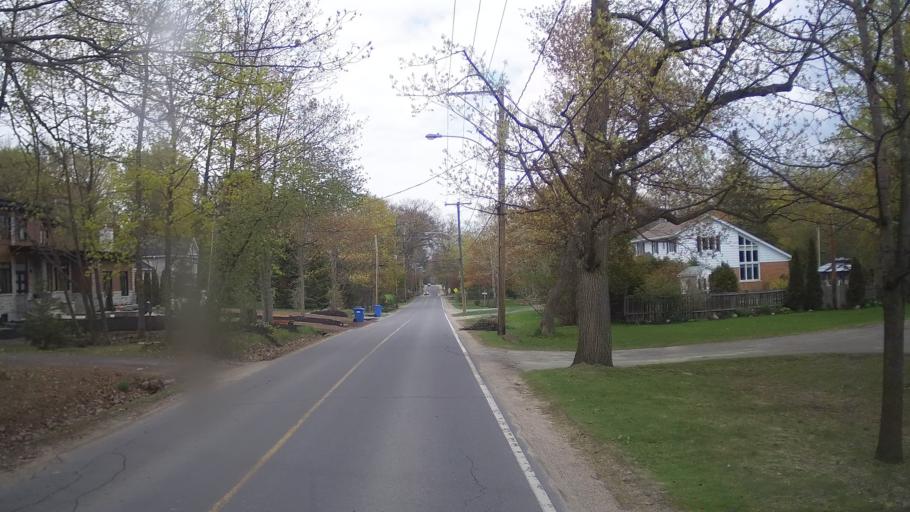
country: CA
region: Quebec
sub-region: Monteregie
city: Hudson
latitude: 45.4600
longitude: -74.1551
